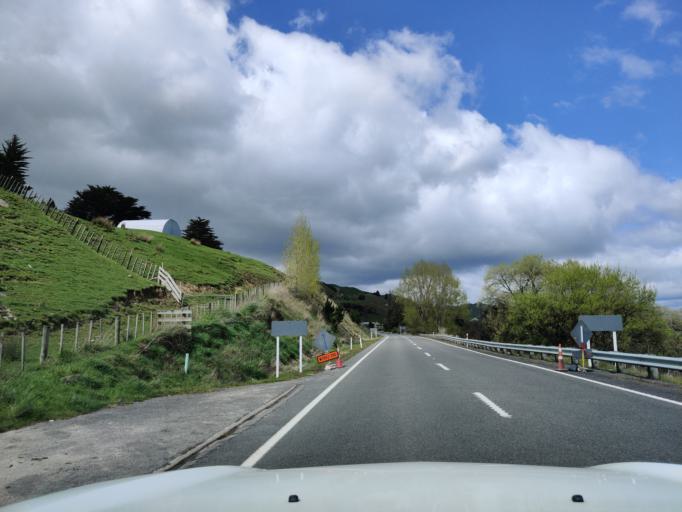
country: NZ
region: Manawatu-Wanganui
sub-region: Ruapehu District
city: Waiouru
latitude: -39.6500
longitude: 175.3254
